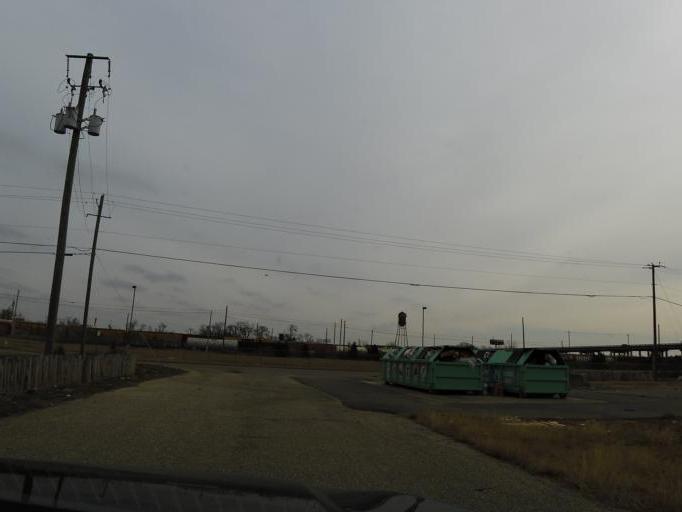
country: US
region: Alabama
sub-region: Montgomery County
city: Montgomery
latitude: 32.3975
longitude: -86.3183
